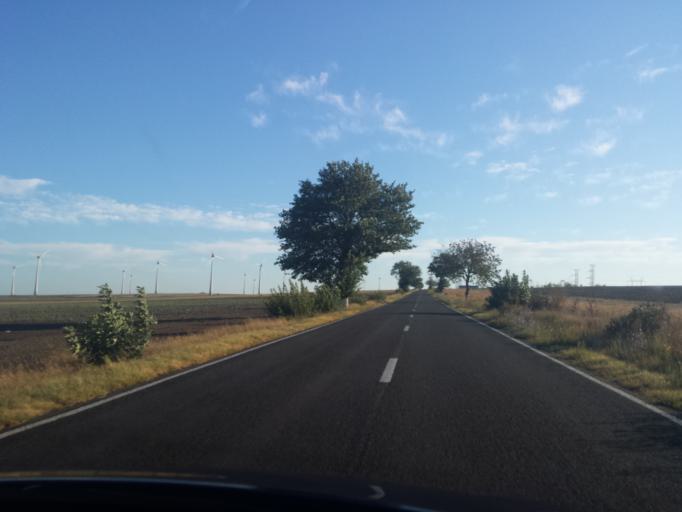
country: RO
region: Constanta
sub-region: Comuna Saraiu
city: Saraiu
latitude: 44.7899
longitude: 28.2358
